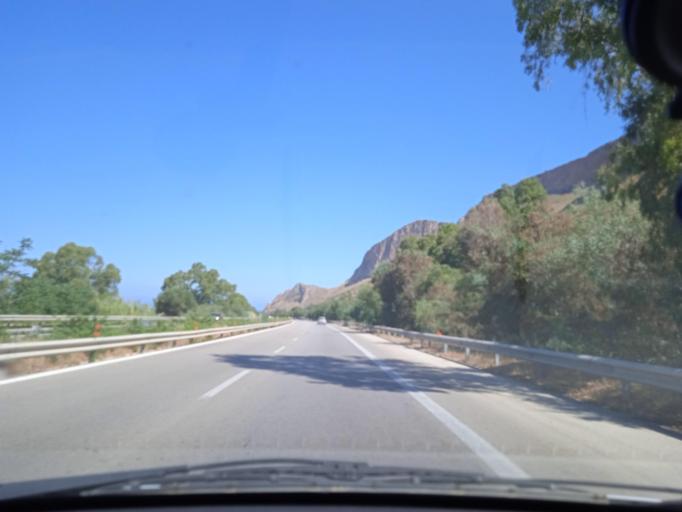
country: IT
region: Sicily
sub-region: Palermo
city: Agliandroni-Paternella
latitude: 38.1106
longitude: 13.0891
